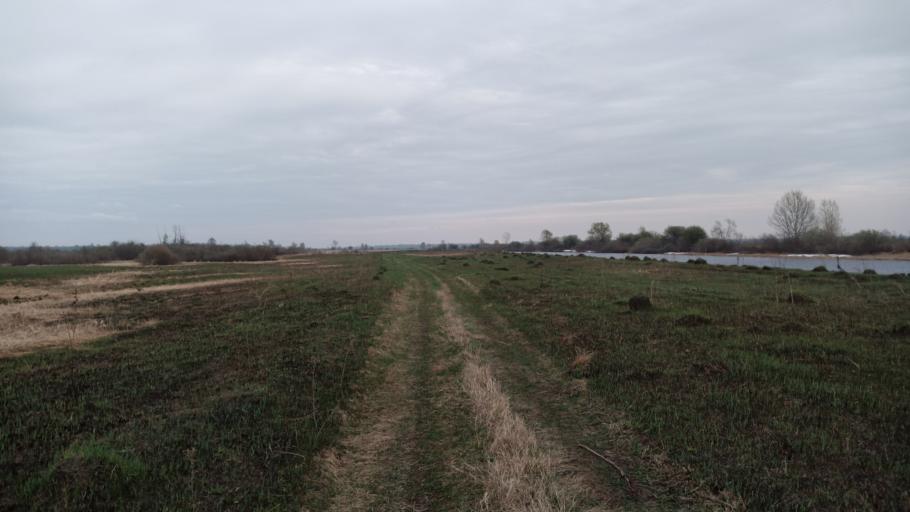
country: RU
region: Altai Krai
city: Yuzhnyy
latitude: 53.2242
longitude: 83.7419
